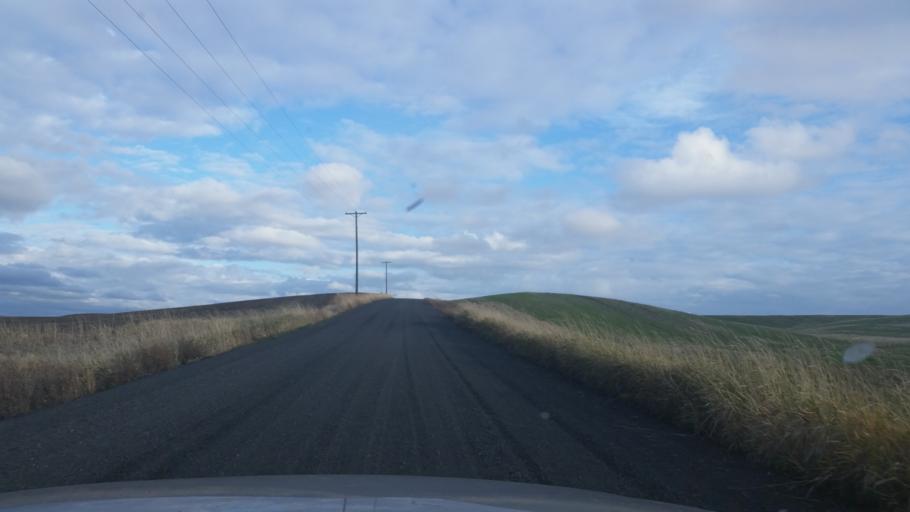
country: US
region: Washington
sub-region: Spokane County
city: Cheney
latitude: 47.4273
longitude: -117.4095
